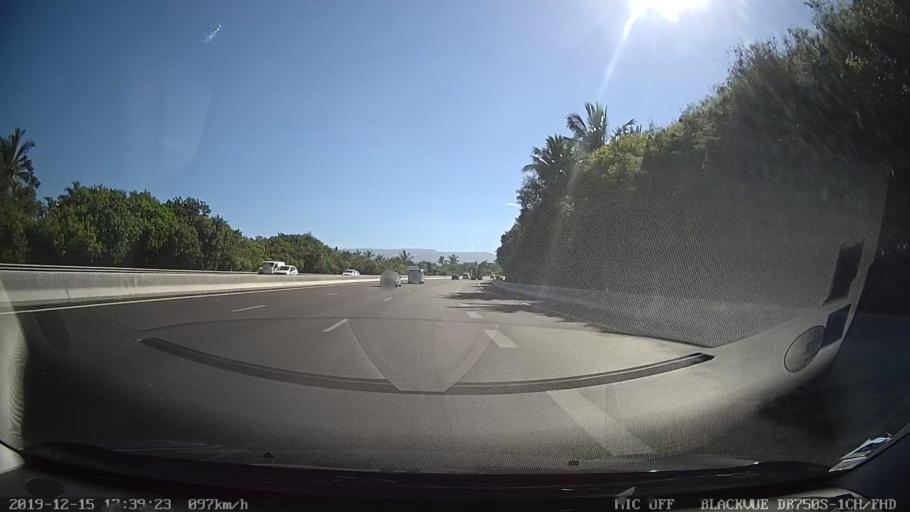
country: RE
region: Reunion
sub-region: Reunion
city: Saint-Pierre
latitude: -21.3231
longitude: 55.4771
